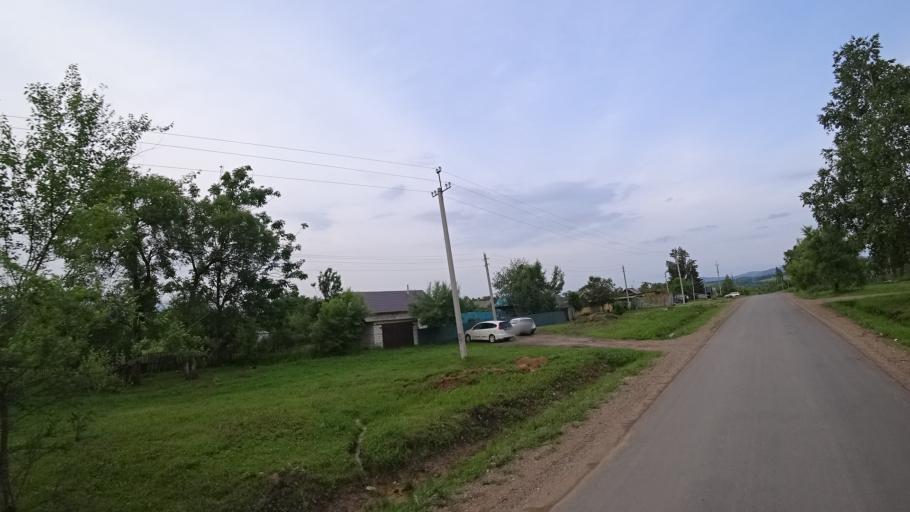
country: RU
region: Primorskiy
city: Novosysoyevka
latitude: 44.2355
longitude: 133.3599
